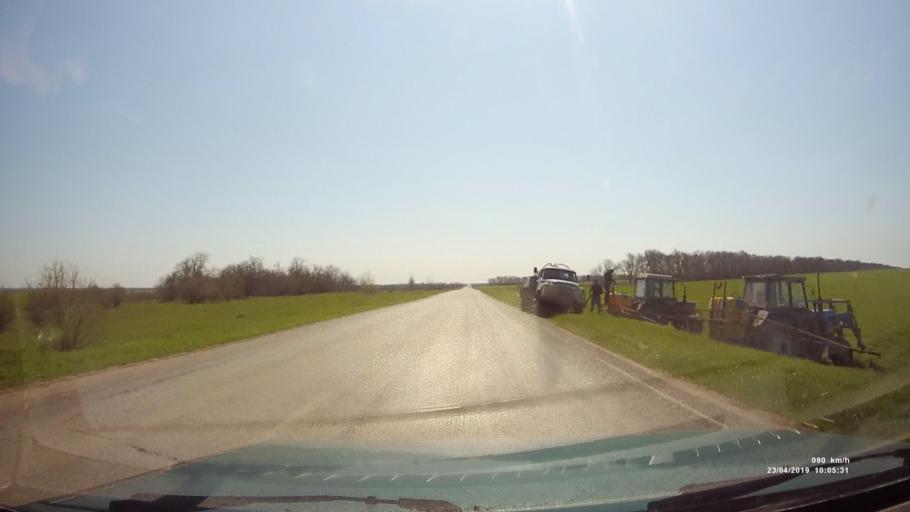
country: RU
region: Rostov
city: Sovetskoye
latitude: 46.7405
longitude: 42.2209
